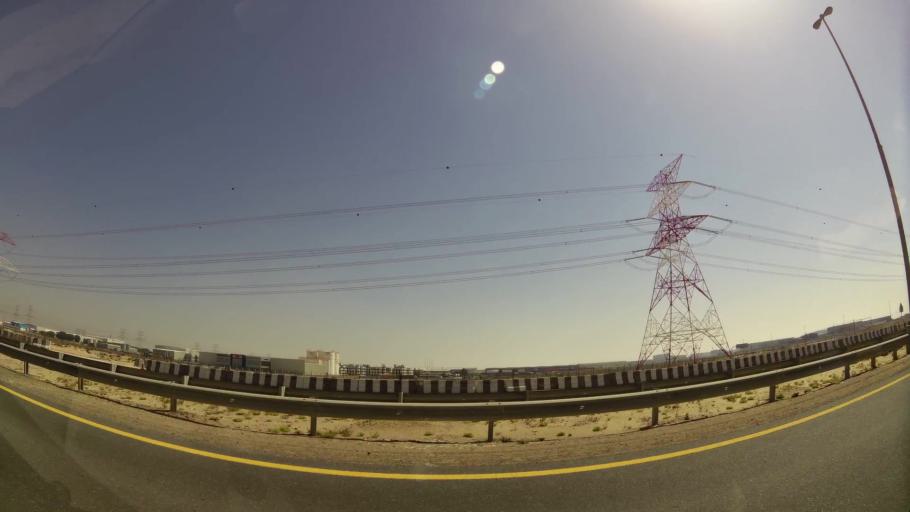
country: AE
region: Dubai
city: Dubai
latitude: 24.9283
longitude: 55.0900
